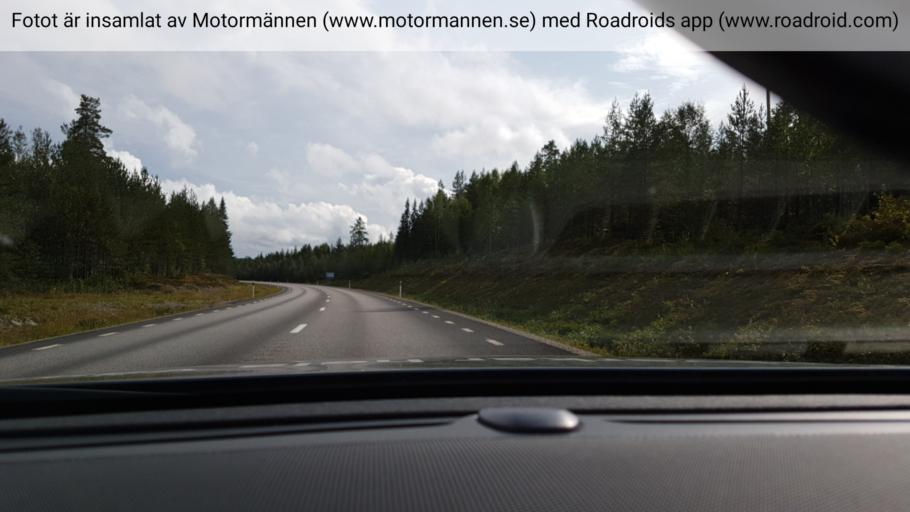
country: SE
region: Dalarna
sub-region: Rattviks Kommun
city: Raettvik
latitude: 60.8039
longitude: 15.2637
